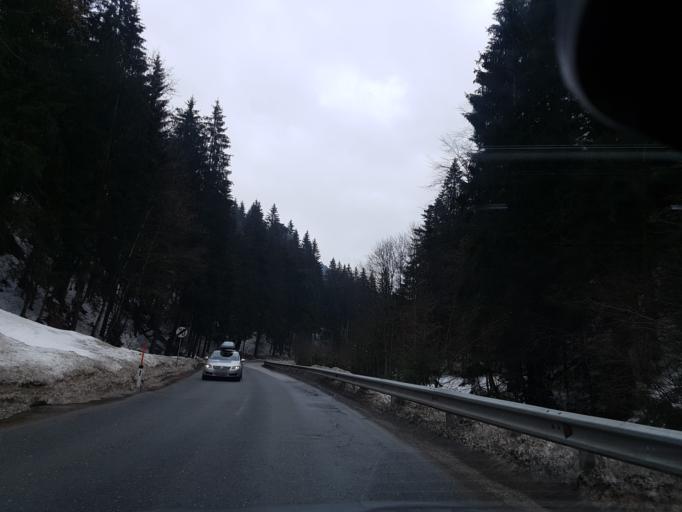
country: AT
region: Tyrol
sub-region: Politischer Bezirk Kufstein
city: Worgl
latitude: 47.4633
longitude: 12.0896
